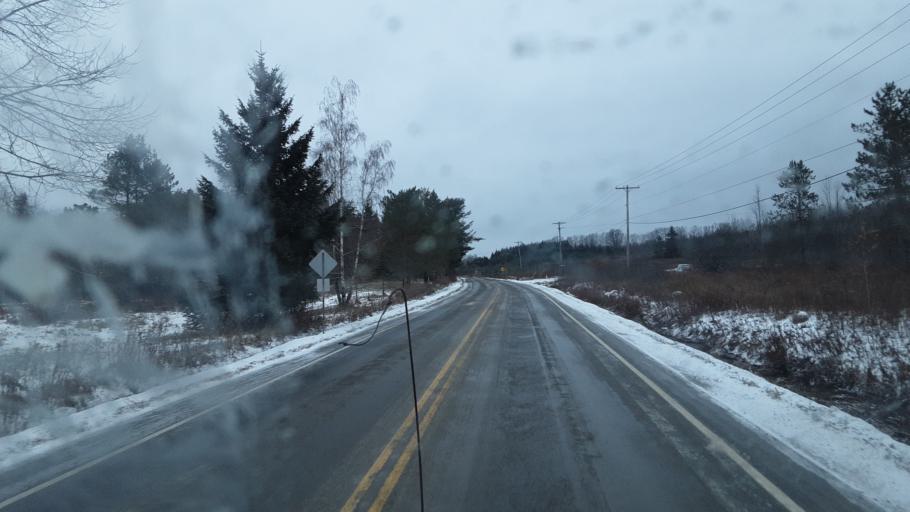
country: US
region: New York
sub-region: Allegany County
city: Friendship
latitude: 42.2320
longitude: -78.1425
